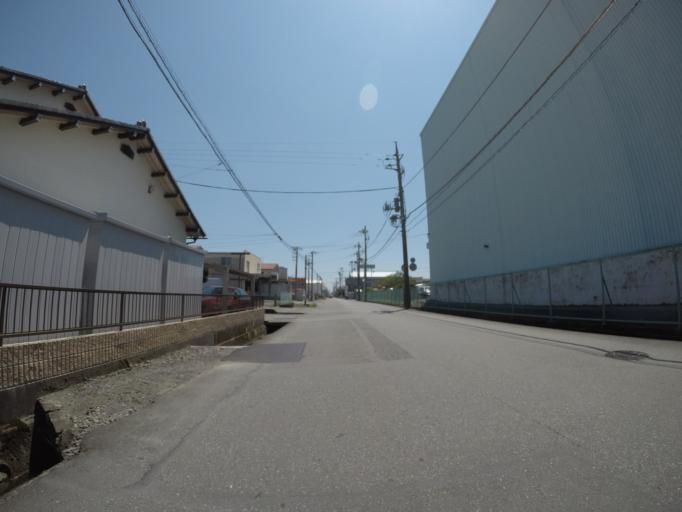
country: JP
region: Shizuoka
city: Fuji
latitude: 35.1377
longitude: 138.6394
